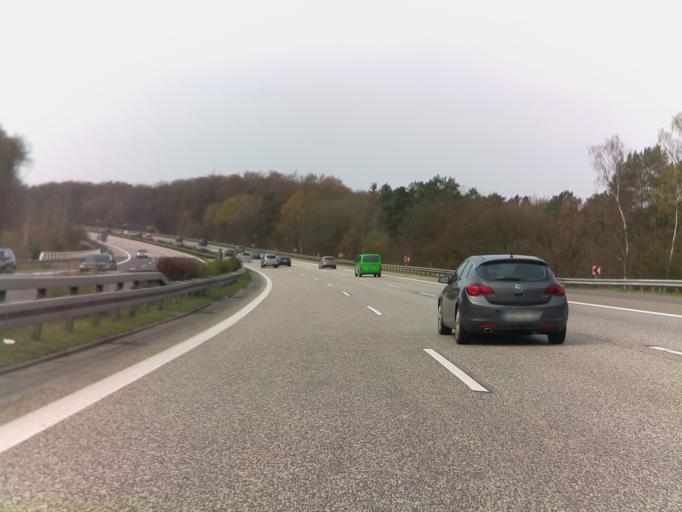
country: DE
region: Brandenburg
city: Niemegk
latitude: 52.0322
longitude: 12.6103
